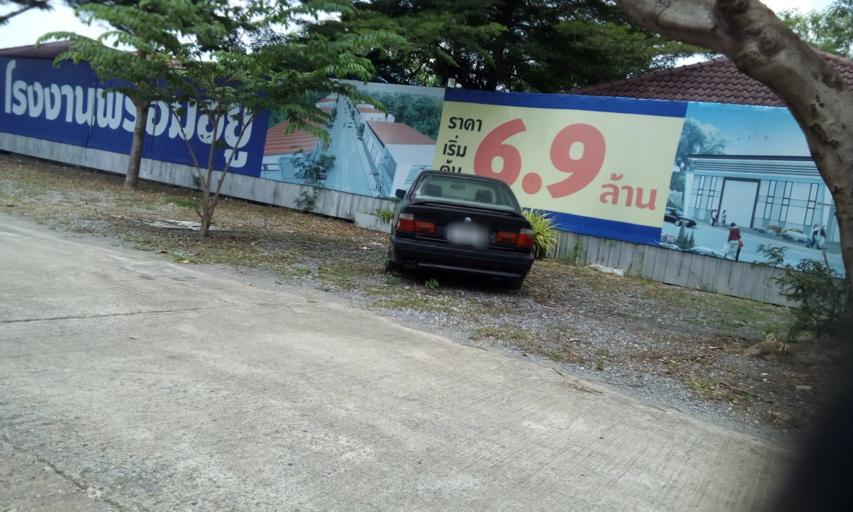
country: TH
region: Pathum Thani
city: Nong Suea
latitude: 14.0687
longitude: 100.8233
